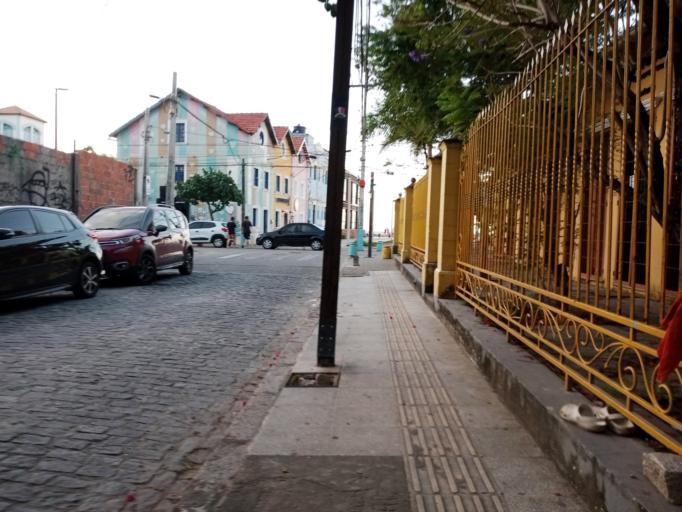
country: BR
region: Ceara
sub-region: Fortaleza
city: Fortaleza
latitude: -3.7197
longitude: -38.5159
